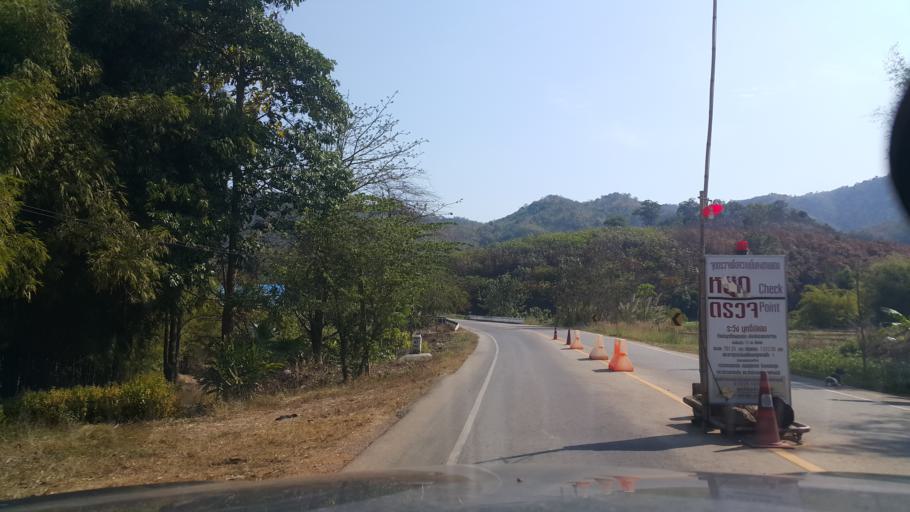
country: TH
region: Loei
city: Pak Chom
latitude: 18.0987
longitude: 102.0314
